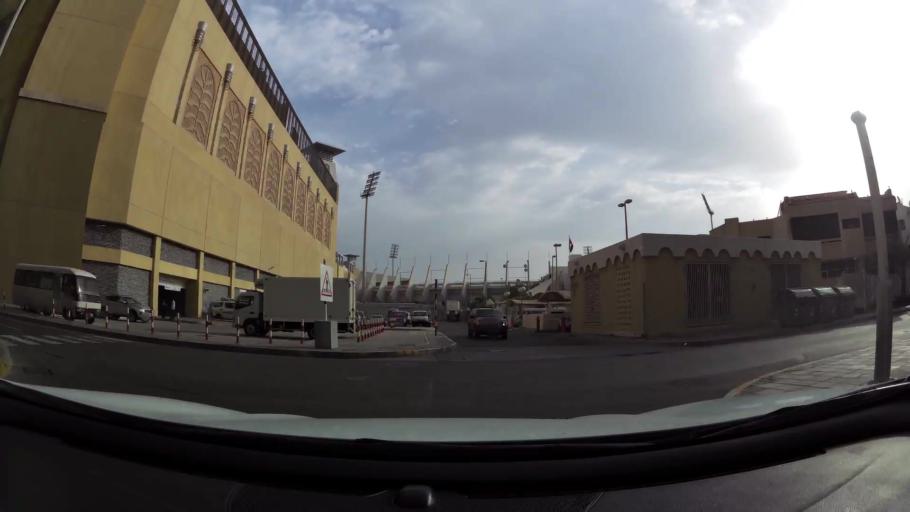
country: AE
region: Abu Dhabi
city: Abu Dhabi
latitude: 24.4684
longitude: 54.3732
